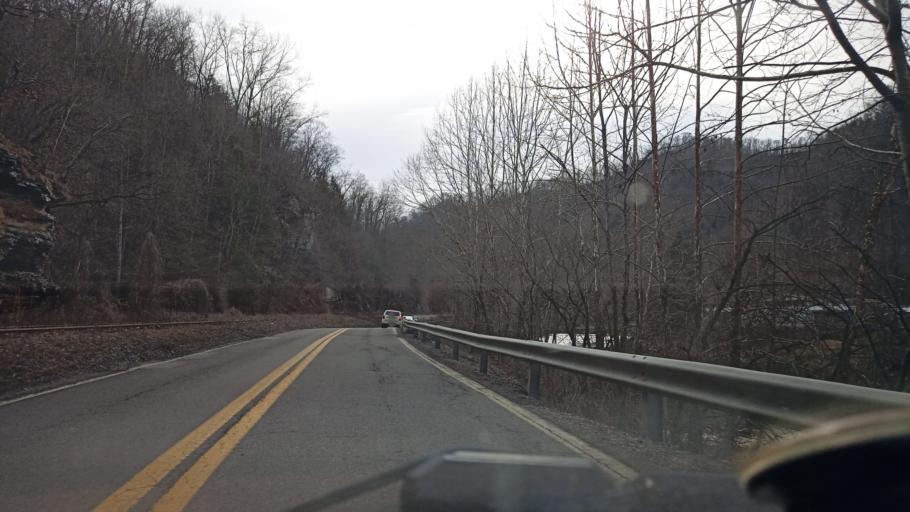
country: US
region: West Virginia
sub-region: Mingo County
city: Gilbert Creek
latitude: 37.6279
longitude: -81.8688
